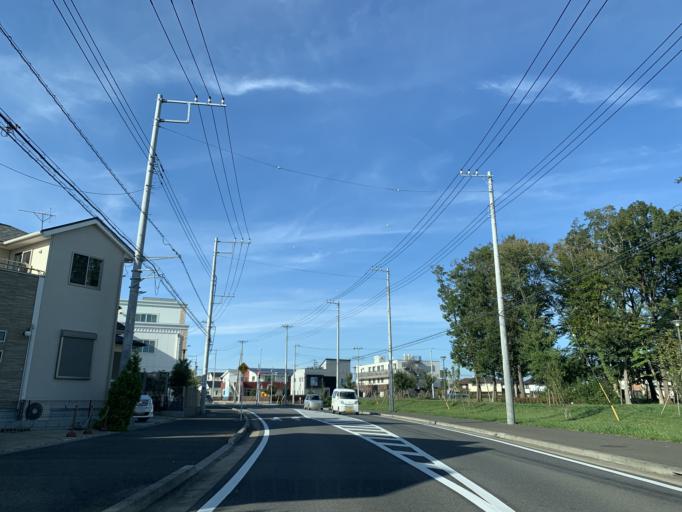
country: JP
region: Chiba
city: Nagareyama
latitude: 35.8786
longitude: 139.9269
